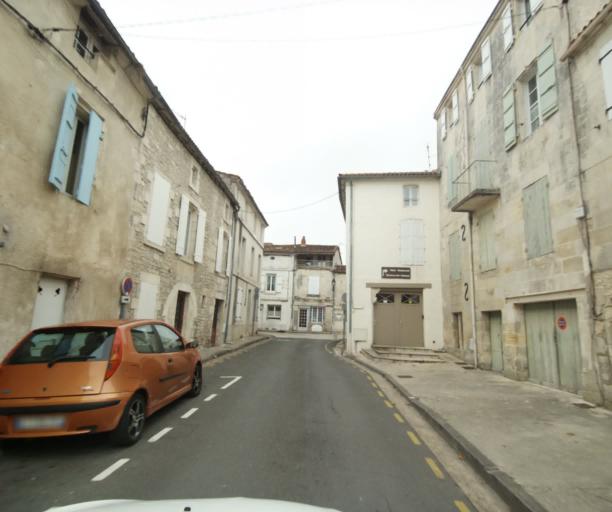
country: FR
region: Poitou-Charentes
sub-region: Departement de la Charente-Maritime
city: Saintes
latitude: 45.7453
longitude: -0.6252
